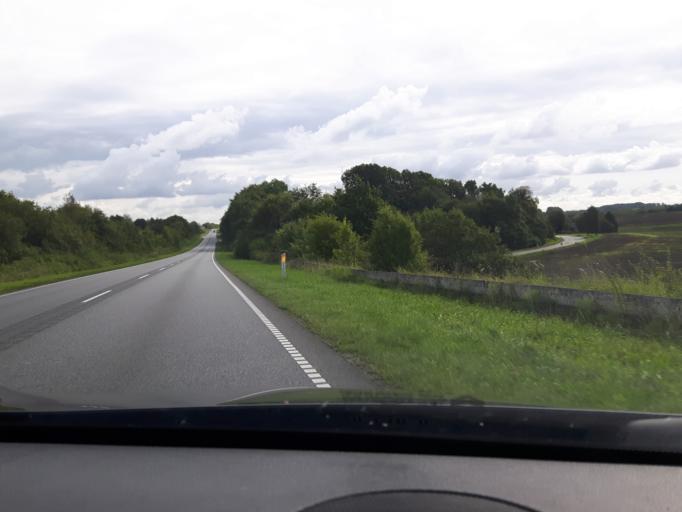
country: DK
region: South Denmark
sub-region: Vejle Kommune
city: Borkop
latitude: 55.6546
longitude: 9.6381
